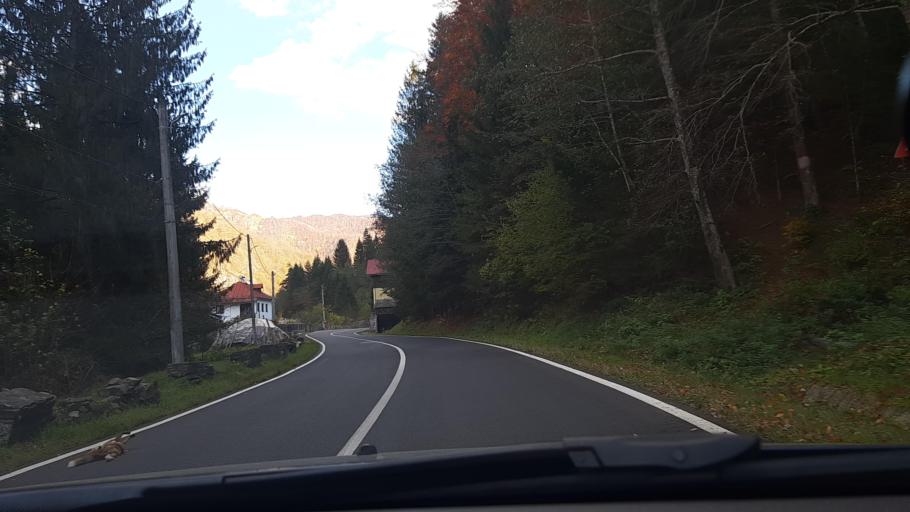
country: RO
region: Valcea
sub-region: Comuna Voineasa
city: Voineasa
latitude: 45.4070
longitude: 23.9759
